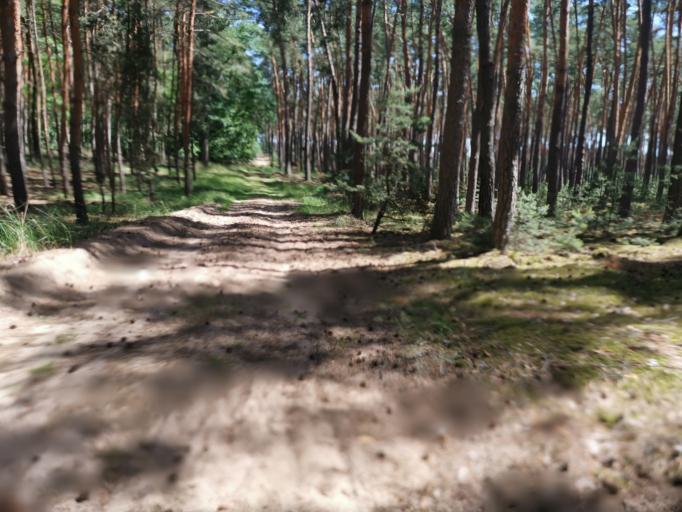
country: CZ
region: South Moravian
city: Bzenec
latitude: 48.9428
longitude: 17.2453
